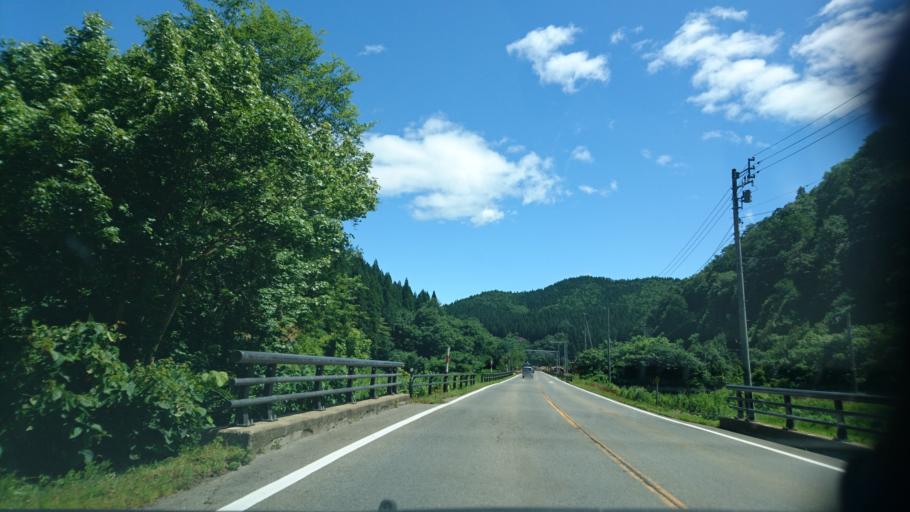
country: JP
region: Akita
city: Kakunodatemachi
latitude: 39.6513
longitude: 140.6681
